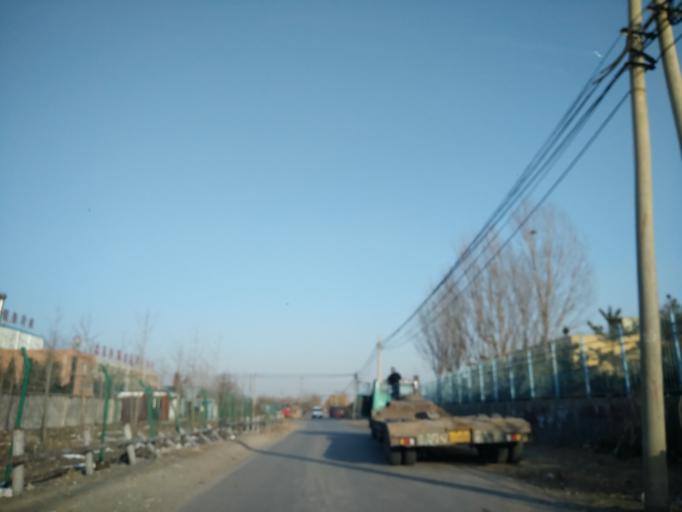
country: CN
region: Beijing
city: Xingfeng
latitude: 39.7216
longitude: 116.3748
